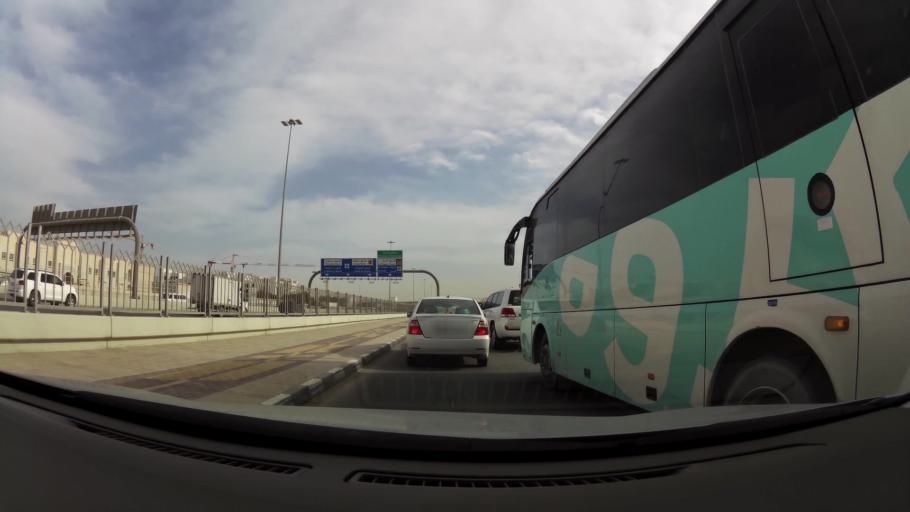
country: QA
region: Baladiyat ar Rayyan
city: Ar Rayyan
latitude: 25.3051
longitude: 51.4729
